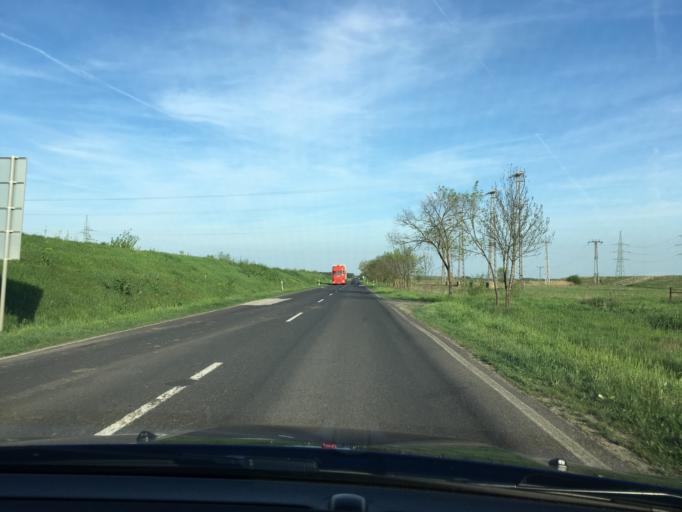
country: HU
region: Bekes
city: Szeghalom
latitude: 47.0111
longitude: 21.1864
